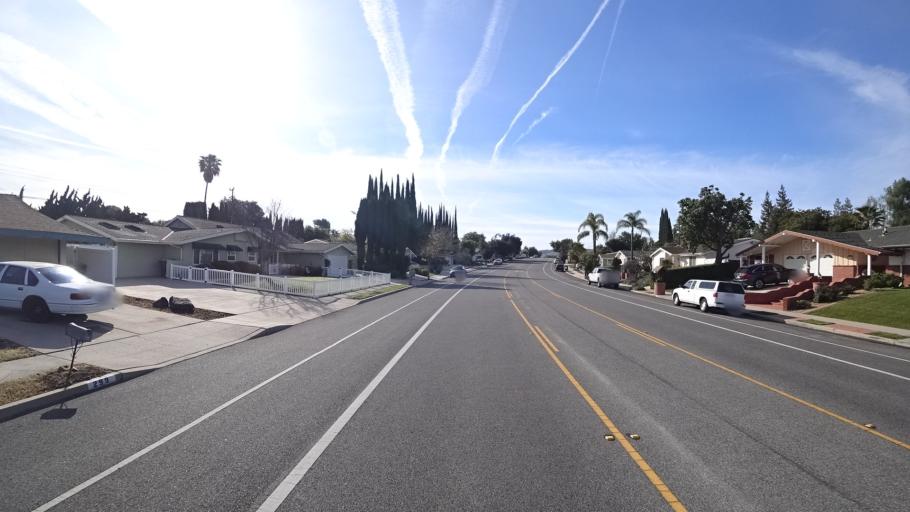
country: US
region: California
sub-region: Ventura County
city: Thousand Oaks
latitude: 34.1936
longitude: -118.8702
